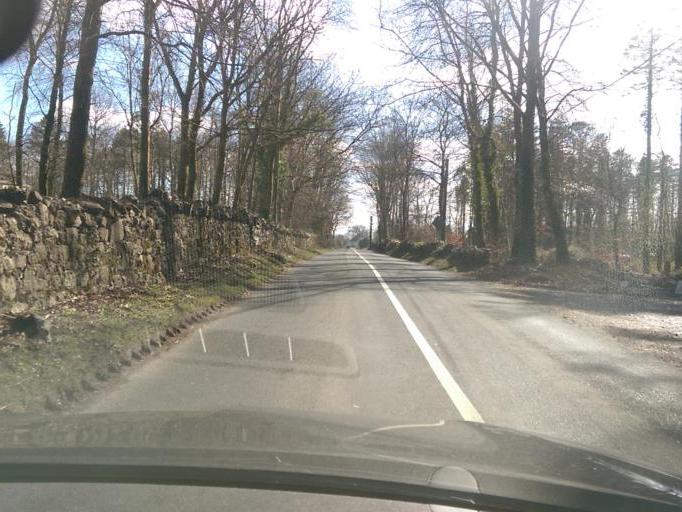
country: IE
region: Connaught
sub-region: County Galway
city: Athenry
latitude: 53.3320
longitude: -8.7686
